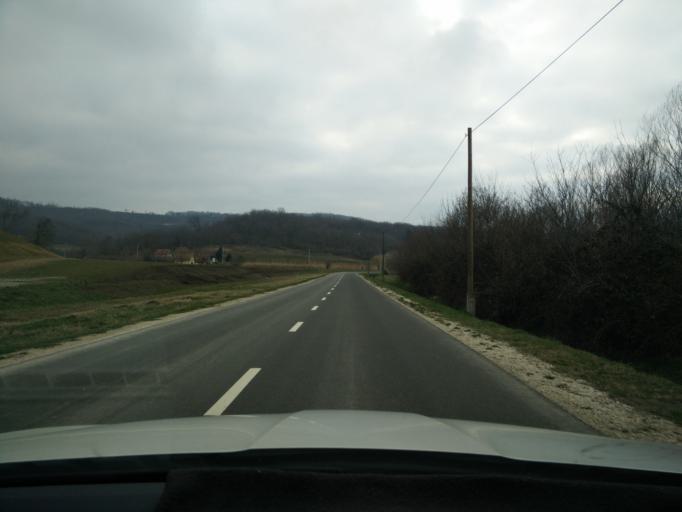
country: HU
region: Tolna
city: Szekszard
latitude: 46.3329
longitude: 18.6703
